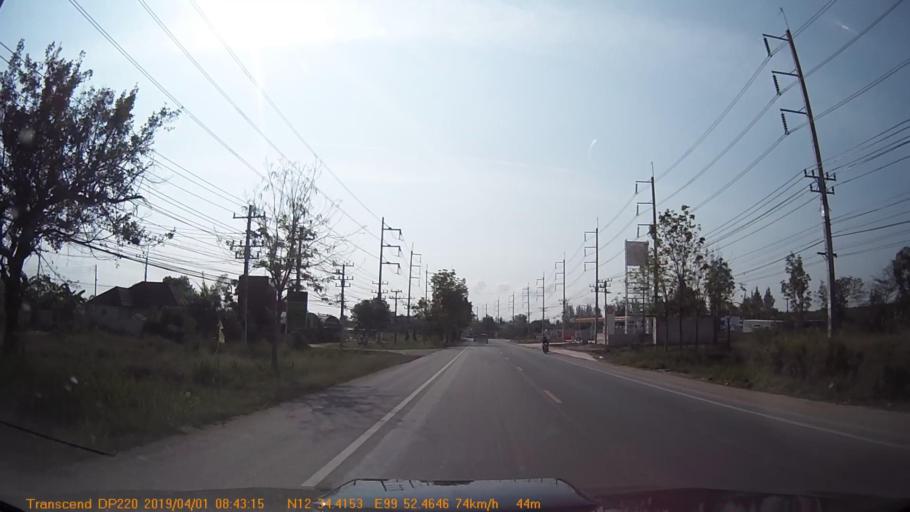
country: TH
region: Prachuap Khiri Khan
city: Hua Hin
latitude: 12.5734
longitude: 99.8748
